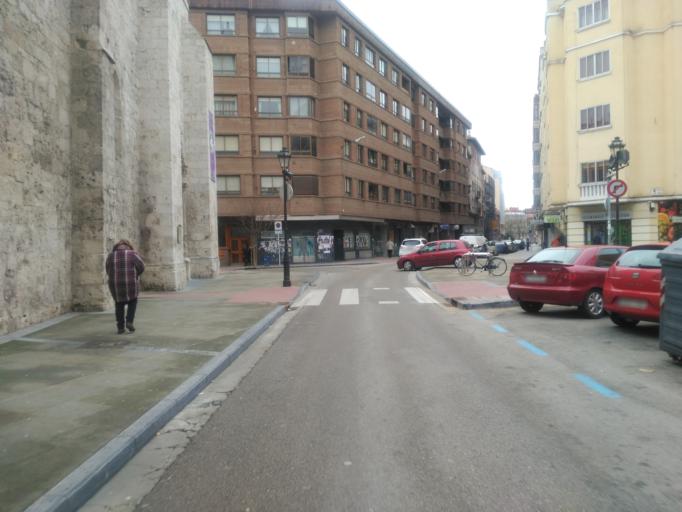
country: ES
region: Castille and Leon
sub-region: Provincia de Burgos
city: Burgos
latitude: 42.3370
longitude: -3.7020
